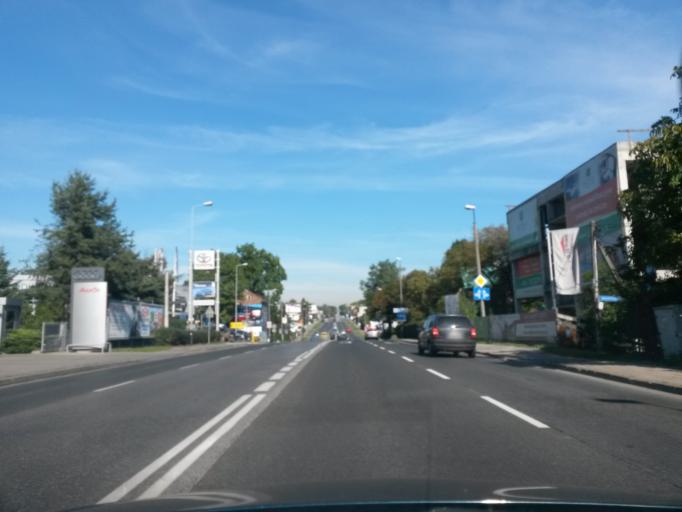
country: PL
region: Lesser Poland Voivodeship
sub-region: Powiat krakowski
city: Libertow
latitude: 49.9980
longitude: 19.9202
